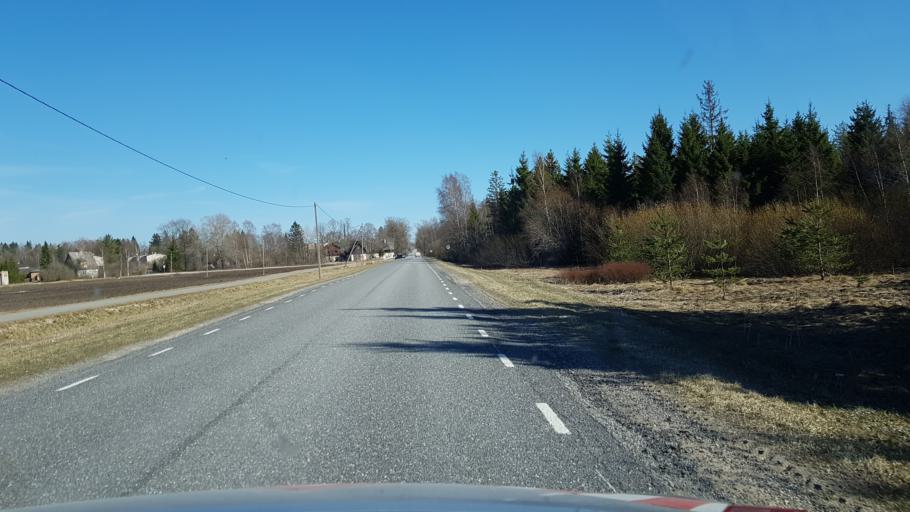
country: EE
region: Laeaene-Virumaa
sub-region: Rakke vald
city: Rakke
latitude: 58.9937
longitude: 26.2226
